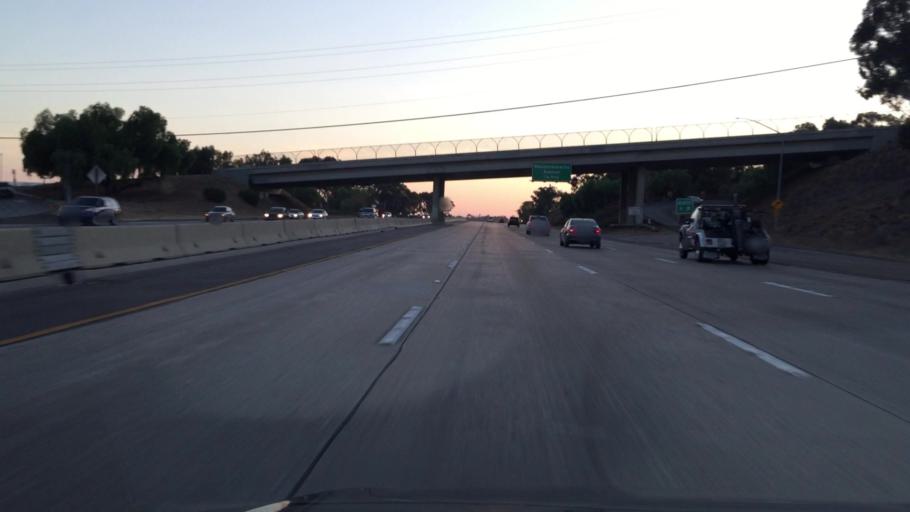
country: US
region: California
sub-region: San Diego County
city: Lemon Grove
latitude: 32.7468
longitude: -117.0299
